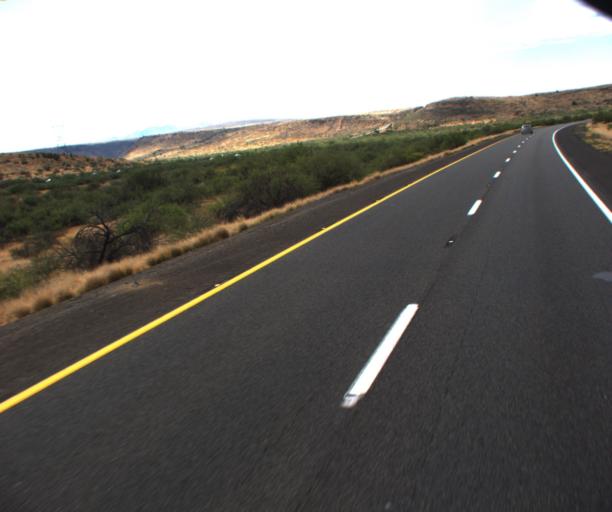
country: US
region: Arizona
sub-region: Yavapai County
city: Cordes Lakes
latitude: 34.2447
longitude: -112.1138
